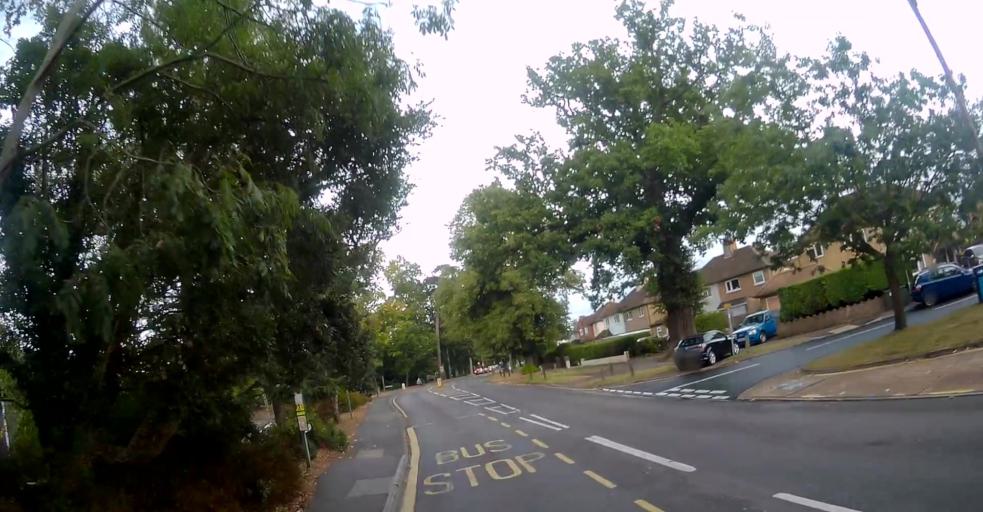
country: GB
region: England
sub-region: Surrey
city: Knaphill
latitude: 51.3124
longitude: -0.6090
